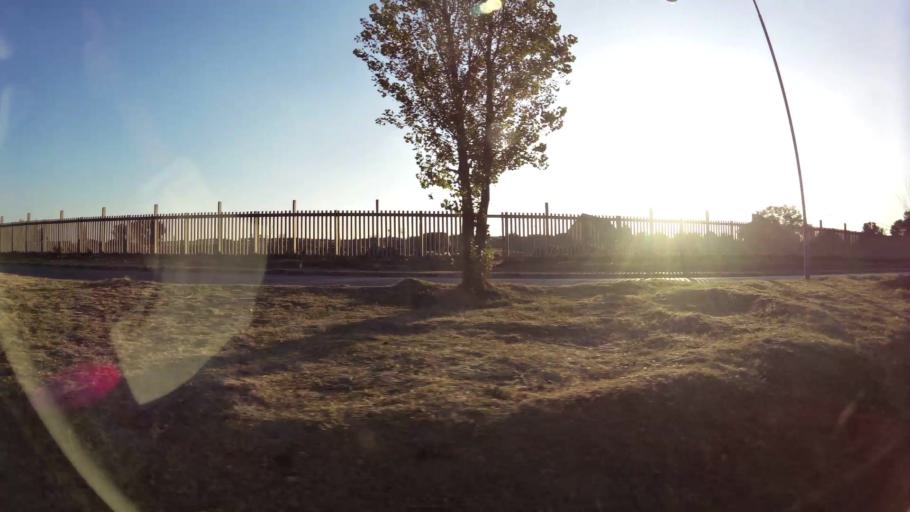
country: ZA
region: Gauteng
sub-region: City of Johannesburg Metropolitan Municipality
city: Soweto
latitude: -26.2469
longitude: 27.8777
